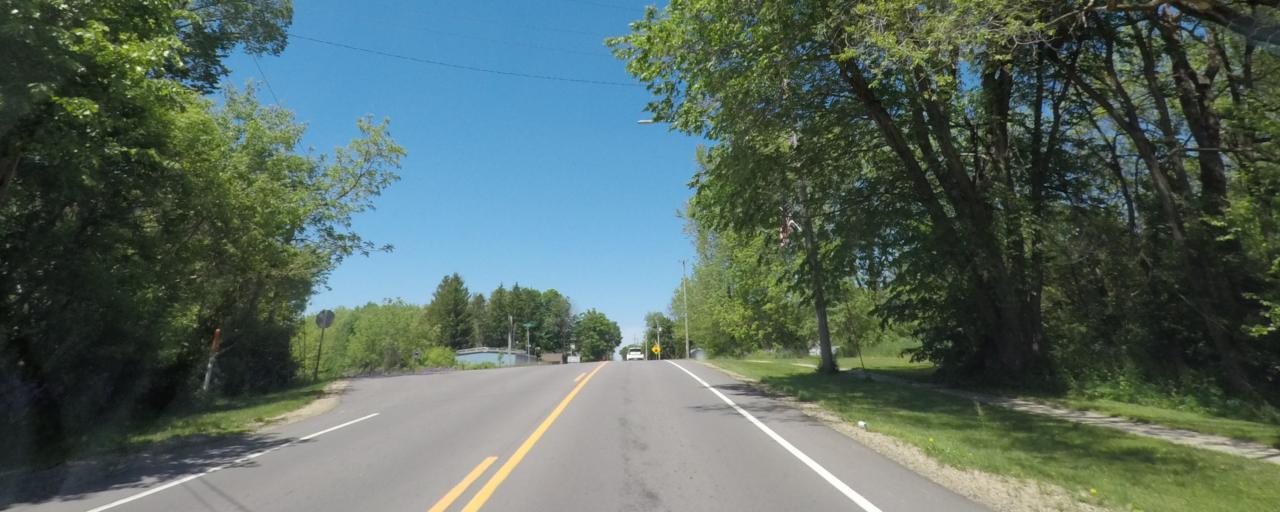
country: US
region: Wisconsin
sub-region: Green County
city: Brooklyn
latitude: 42.8498
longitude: -89.3692
